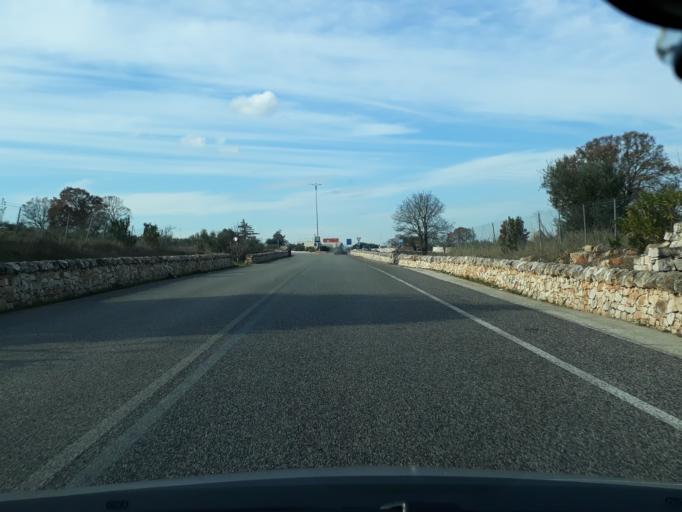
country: IT
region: Apulia
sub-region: Provincia di Bari
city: Locorotondo
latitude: 40.7609
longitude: 17.3345
